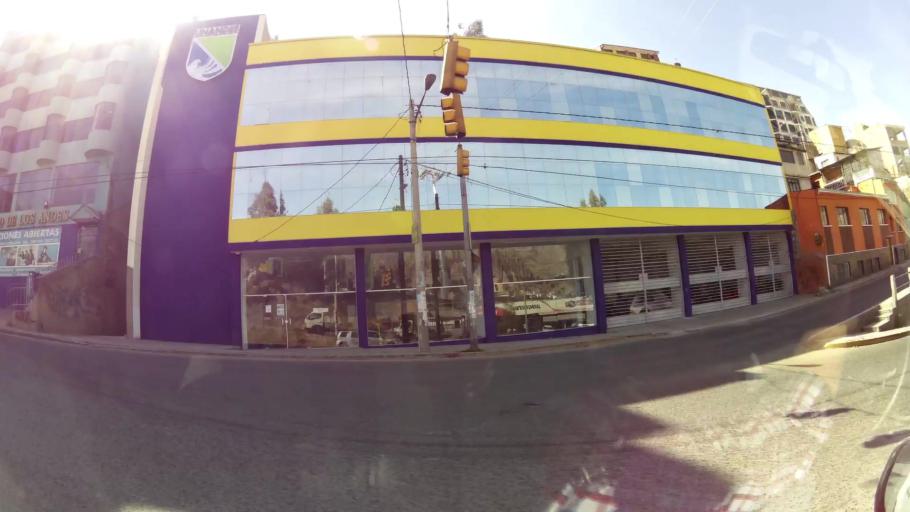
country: BO
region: La Paz
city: La Paz
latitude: -16.5194
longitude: -68.1146
